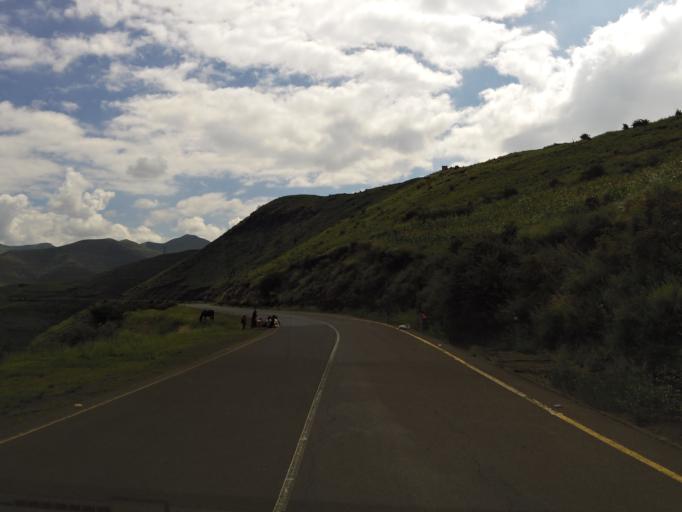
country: LS
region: Thaba-Tseka
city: Thaba-Tseka
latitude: -29.1481
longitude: 28.4896
